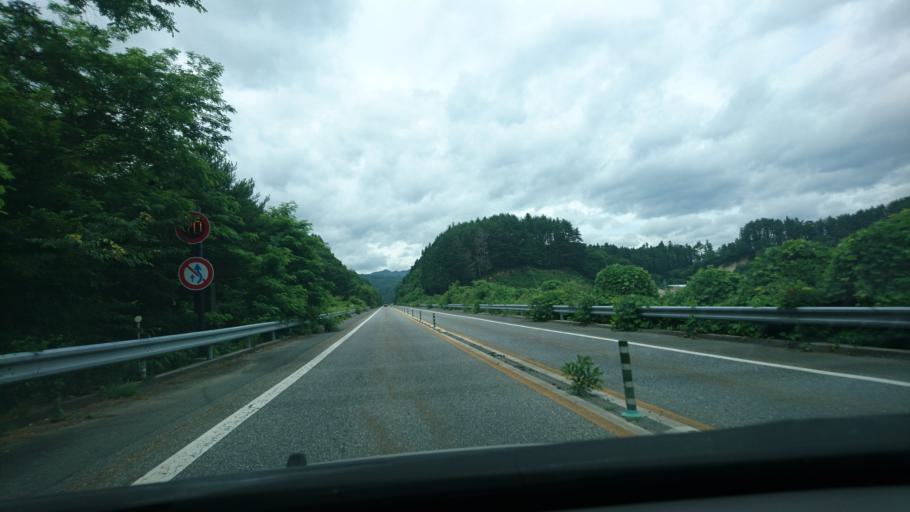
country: JP
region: Iwate
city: Yamada
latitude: 39.4520
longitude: 141.9509
